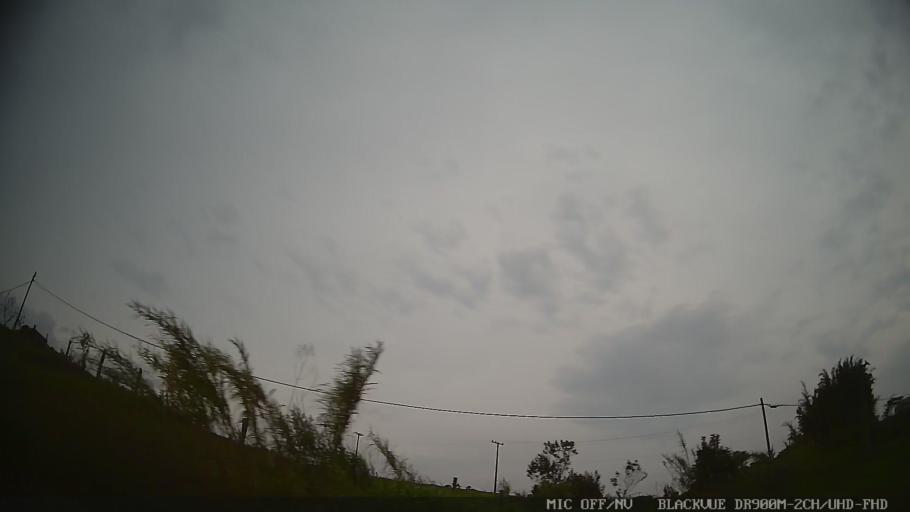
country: BR
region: Sao Paulo
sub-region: Braganca Paulista
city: Braganca Paulista
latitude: -22.9618
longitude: -46.5863
